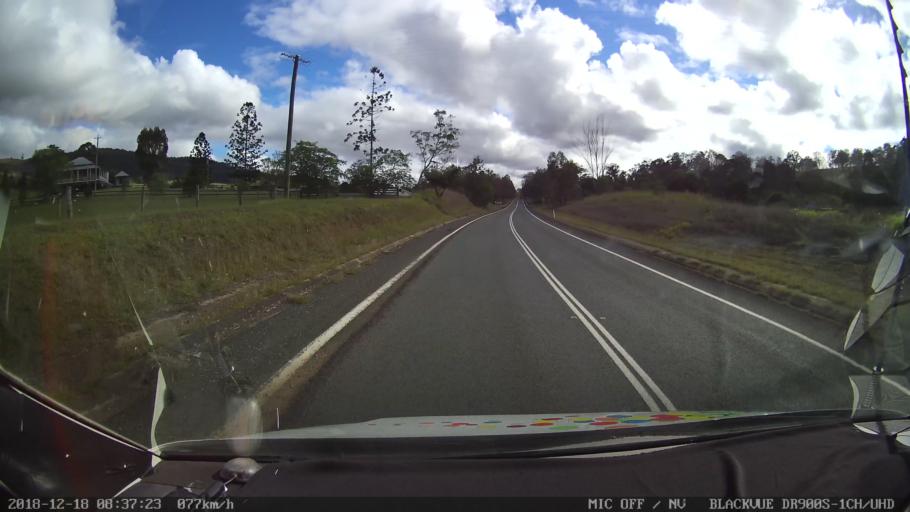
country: AU
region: New South Wales
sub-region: Kyogle
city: Kyogle
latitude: -28.2645
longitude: 152.8170
